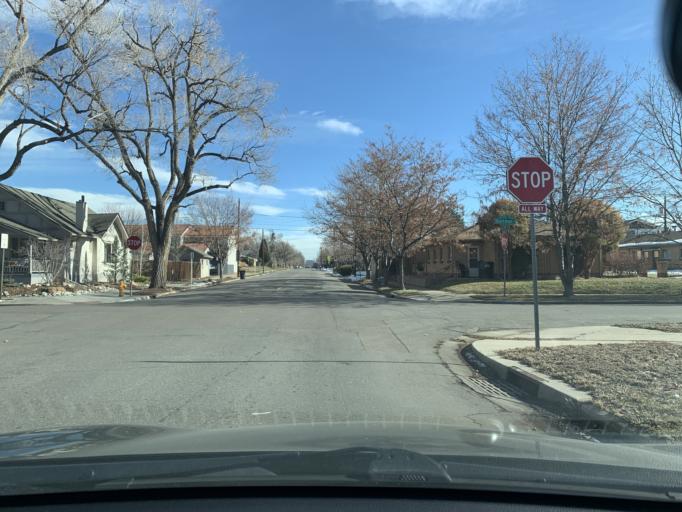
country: US
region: Colorado
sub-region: Jefferson County
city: Edgewater
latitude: 39.7512
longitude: -105.0407
